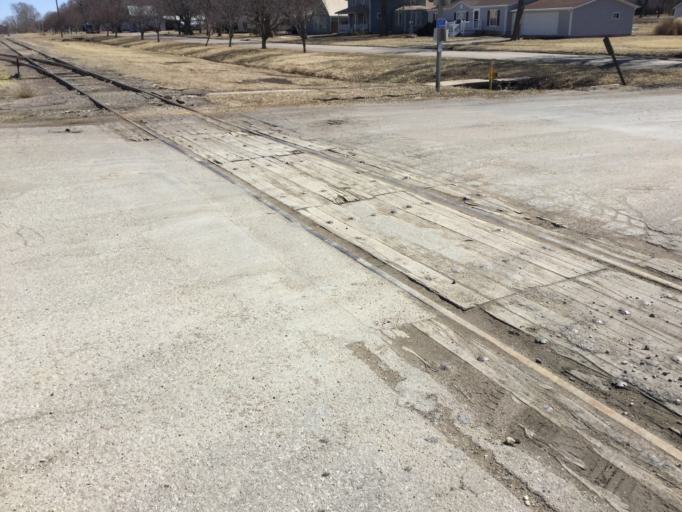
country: US
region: Kansas
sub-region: Marshall County
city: Blue Rapids
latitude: 39.6912
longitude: -96.7494
